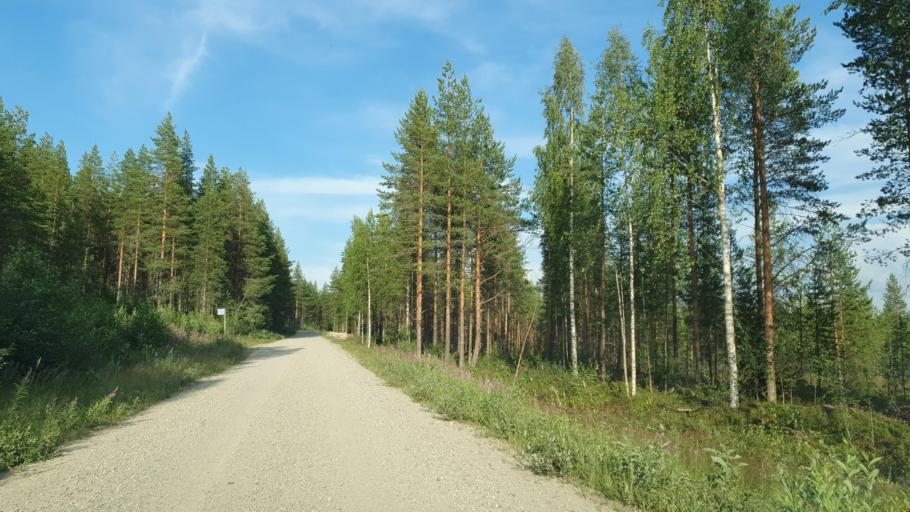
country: FI
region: Kainuu
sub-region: Kehys-Kainuu
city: Kuhmo
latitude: 64.2849
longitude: 29.7643
